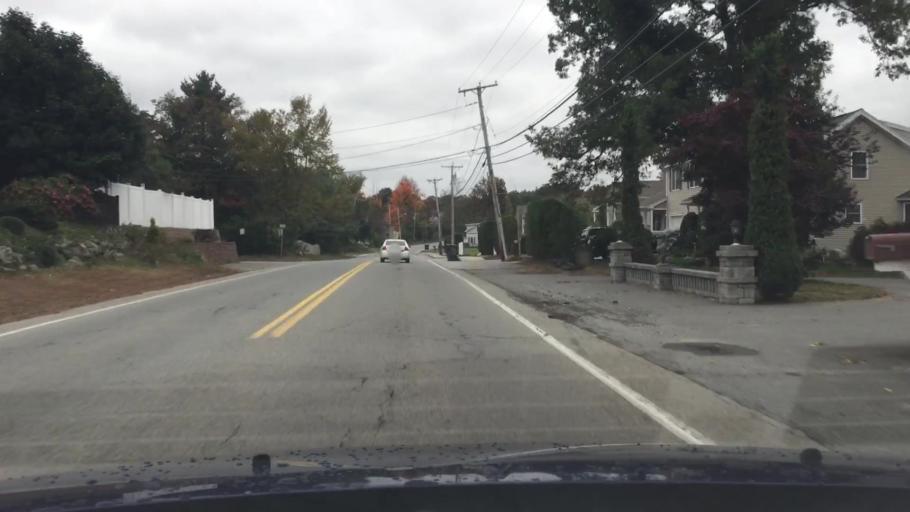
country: US
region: Massachusetts
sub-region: Middlesex County
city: Tyngsboro
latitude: 42.6810
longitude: -71.3674
